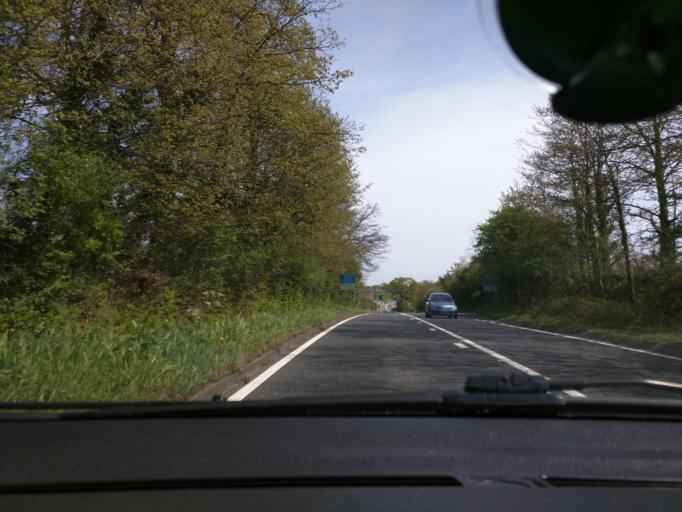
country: GB
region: England
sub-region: Suffolk
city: Saxmundham
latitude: 52.2703
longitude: 1.5201
